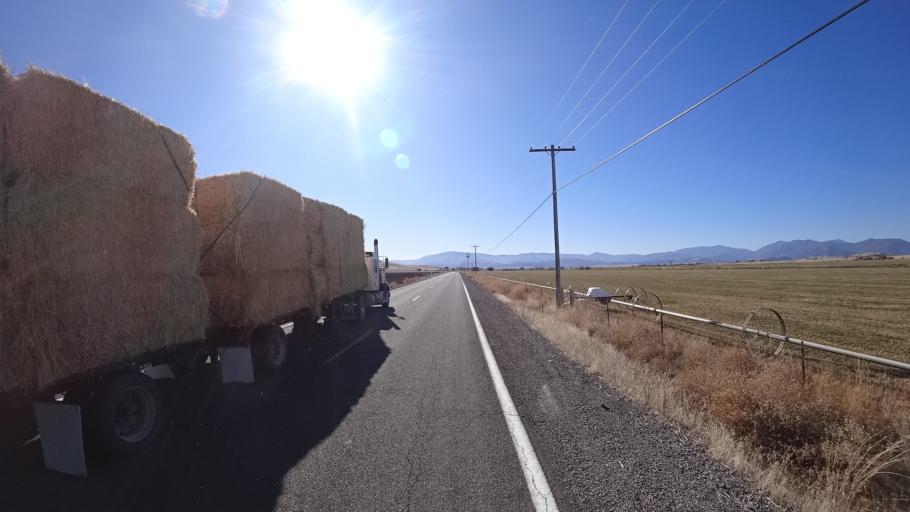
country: US
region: California
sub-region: Siskiyou County
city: Montague
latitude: 41.7625
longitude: -122.4888
